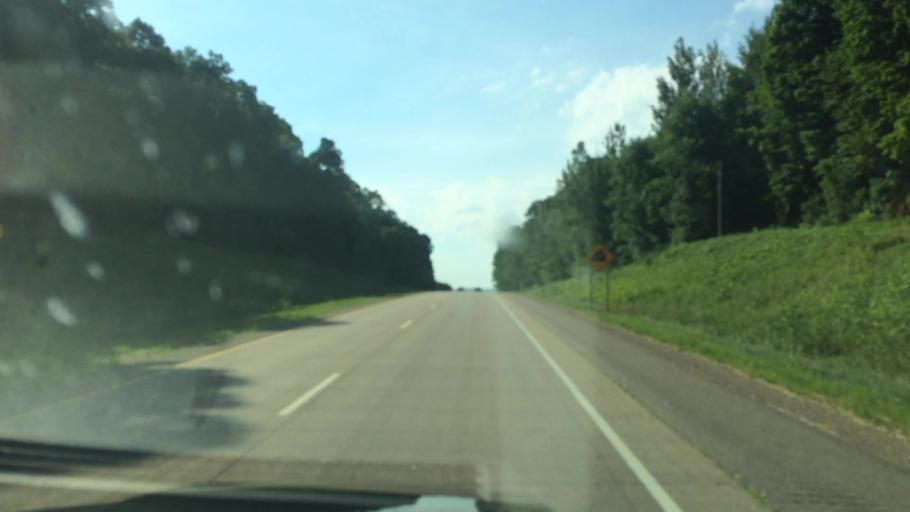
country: US
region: Wisconsin
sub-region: Shawano County
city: Wittenberg
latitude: 44.8219
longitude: -89.0577
